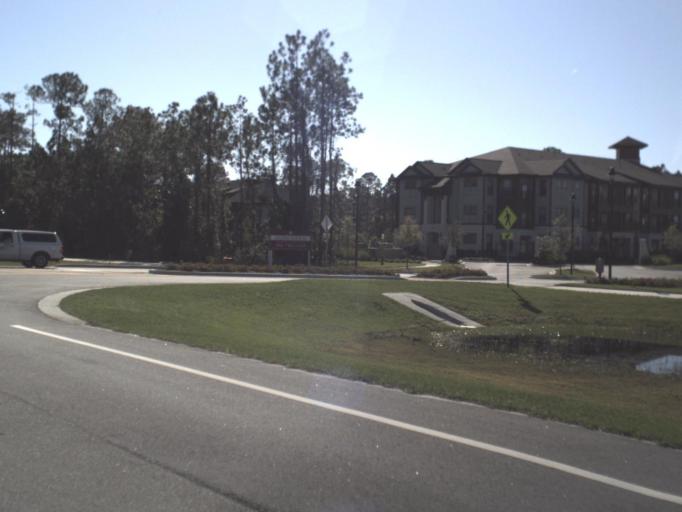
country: US
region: Florida
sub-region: Volusia County
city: Port Orange
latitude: 29.1115
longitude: -81.0402
